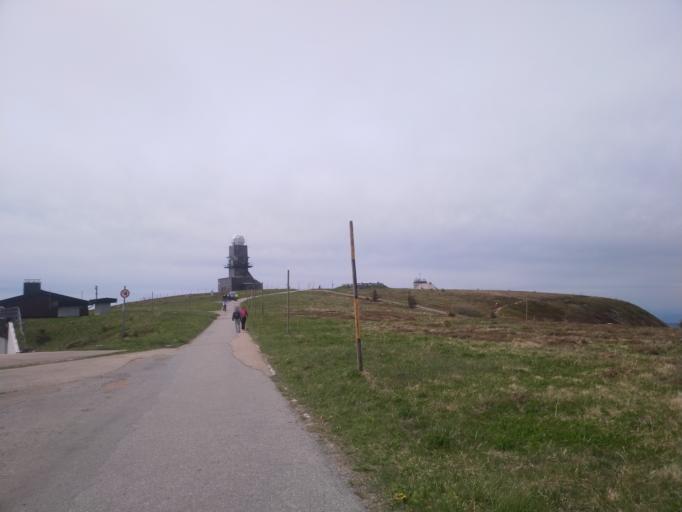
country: DE
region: Baden-Wuerttemberg
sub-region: Freiburg Region
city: Todtnau
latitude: 47.8728
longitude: 8.0069
